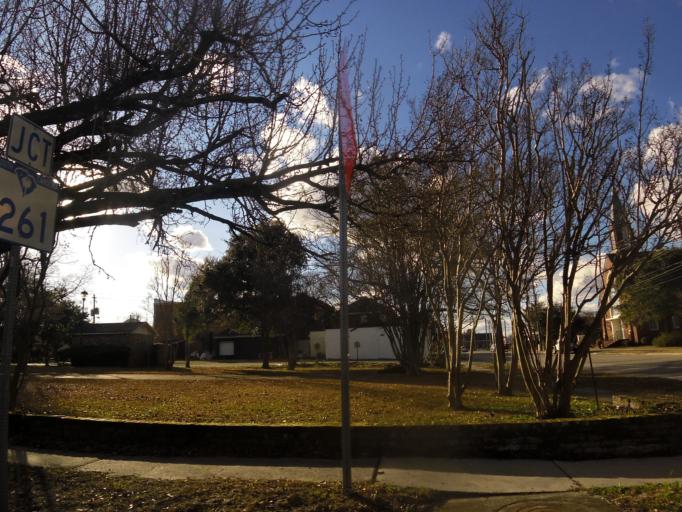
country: US
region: South Carolina
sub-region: Clarendon County
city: Manning
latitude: 33.6965
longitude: -80.2091
